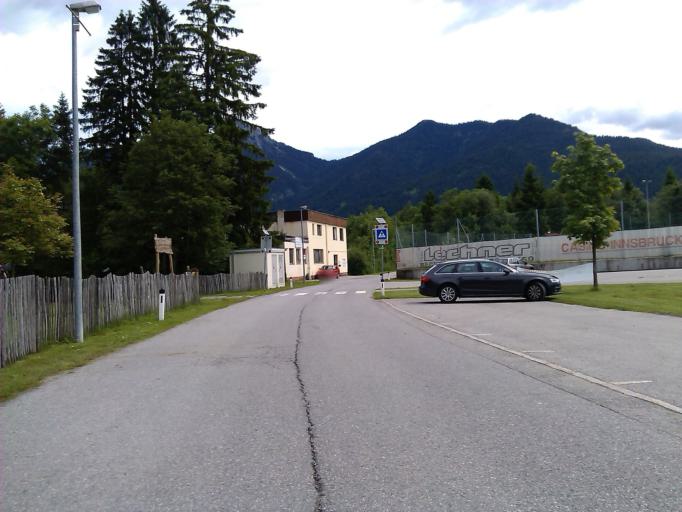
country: AT
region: Tyrol
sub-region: Politischer Bezirk Reutte
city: Lechaschau
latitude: 47.4996
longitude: 10.7075
